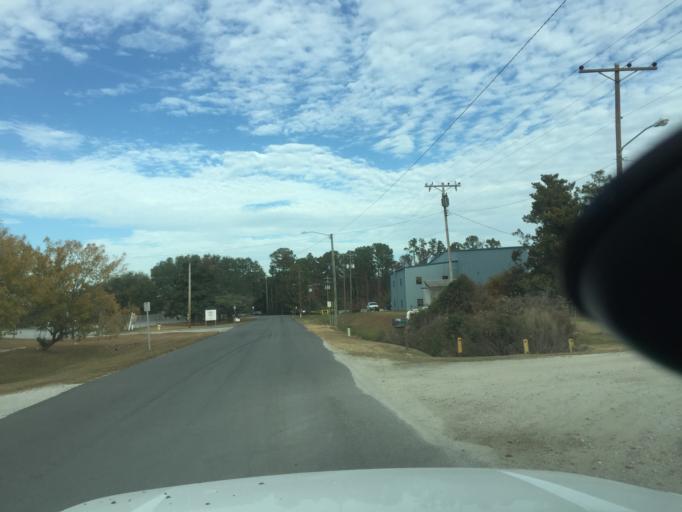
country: US
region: Georgia
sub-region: Chatham County
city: Garden City
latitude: 32.0821
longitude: -81.1463
